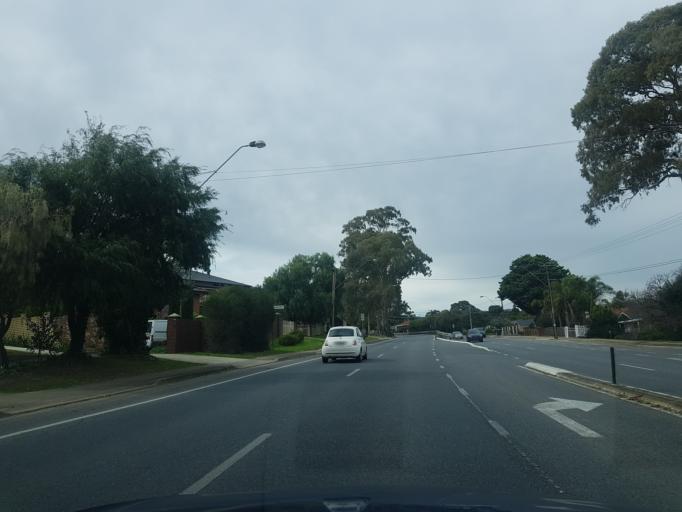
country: AU
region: South Australia
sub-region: Campbelltown
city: Athelstone
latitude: -34.8583
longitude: 138.6878
